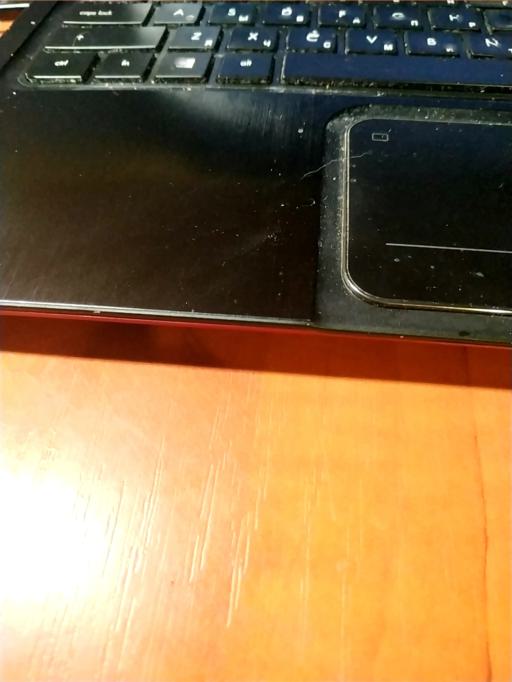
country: RU
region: Tverskaya
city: Ves'yegonsk
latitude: 58.7982
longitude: 37.5436
